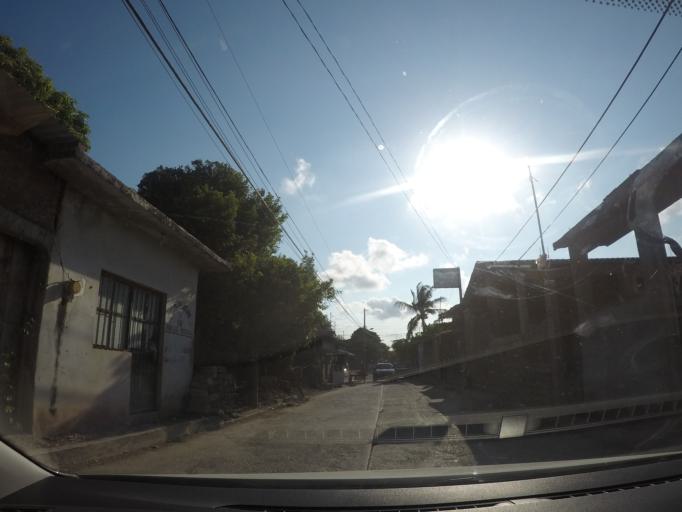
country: MX
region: Oaxaca
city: Juchitan de Zaragoza
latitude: 16.4218
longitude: -95.0264
